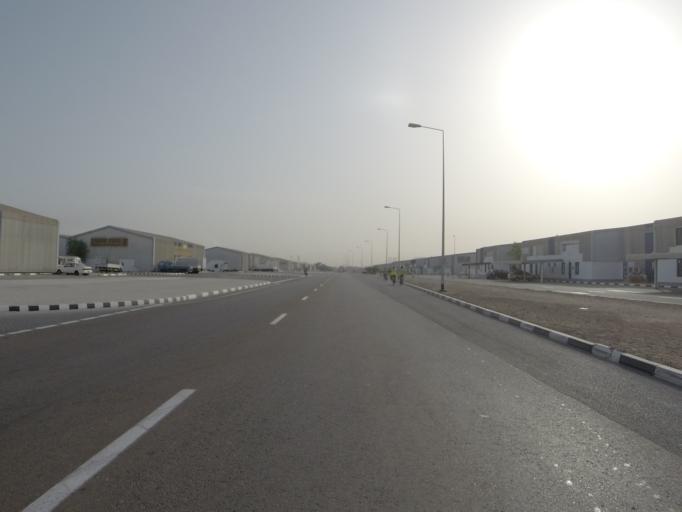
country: AE
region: Dubai
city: Dubai
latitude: 24.9607
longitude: 55.0607
